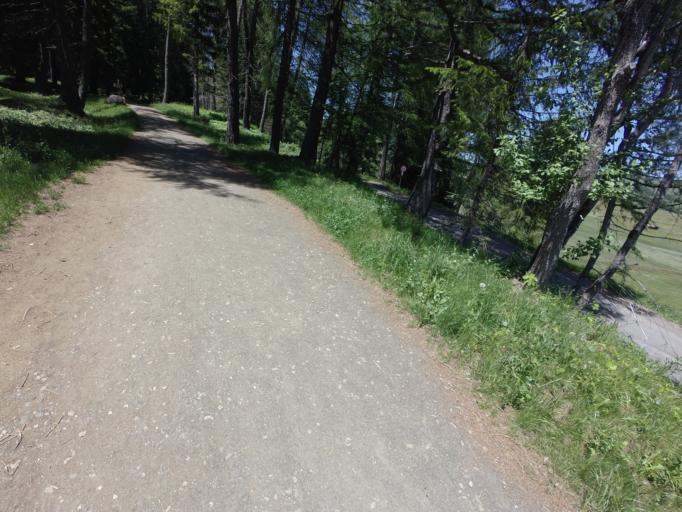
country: IT
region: Trentino-Alto Adige
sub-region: Bolzano
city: Ortisei
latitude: 46.5380
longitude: 11.6528
